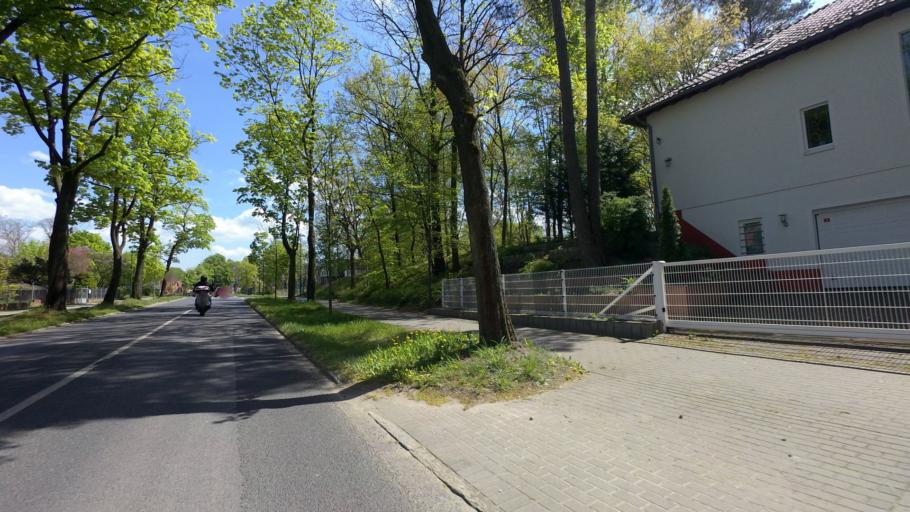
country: DE
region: Berlin
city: Blankenfelde
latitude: 52.6368
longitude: 13.3716
